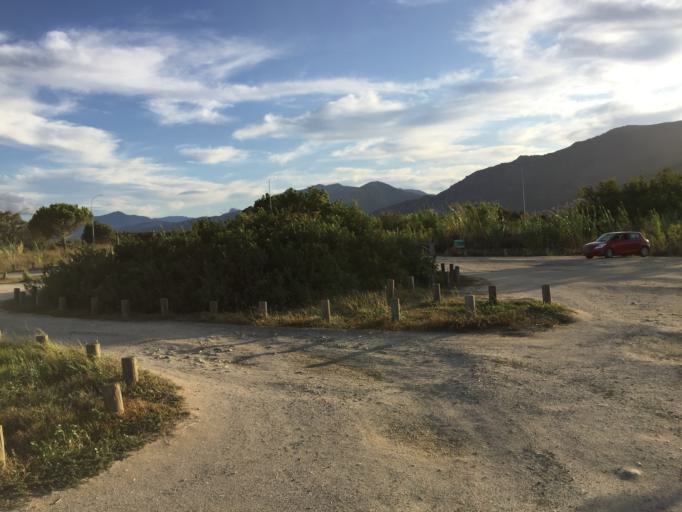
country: FR
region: Corsica
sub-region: Departement de la Haute-Corse
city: Biguglia
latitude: 42.6552
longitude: 9.4502
